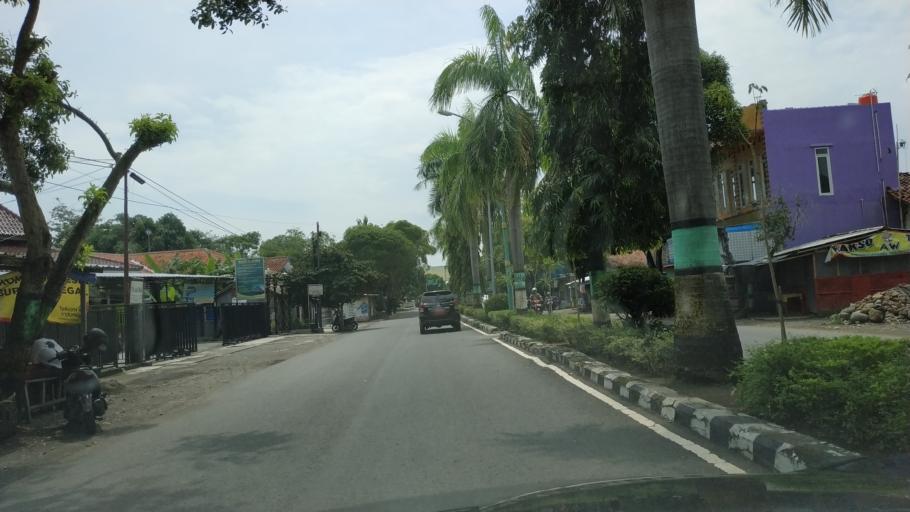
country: ID
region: Central Java
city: Slawi
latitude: -6.9821
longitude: 109.1270
